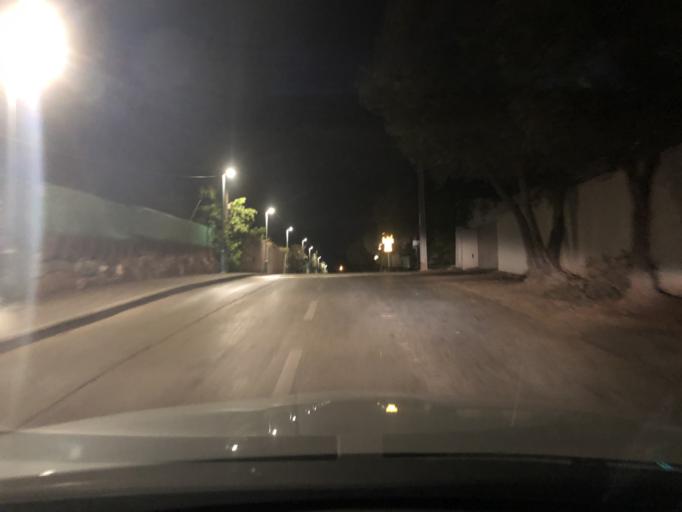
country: IL
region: Central District
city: Hod HaSharon
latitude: 32.1681
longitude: 34.8970
